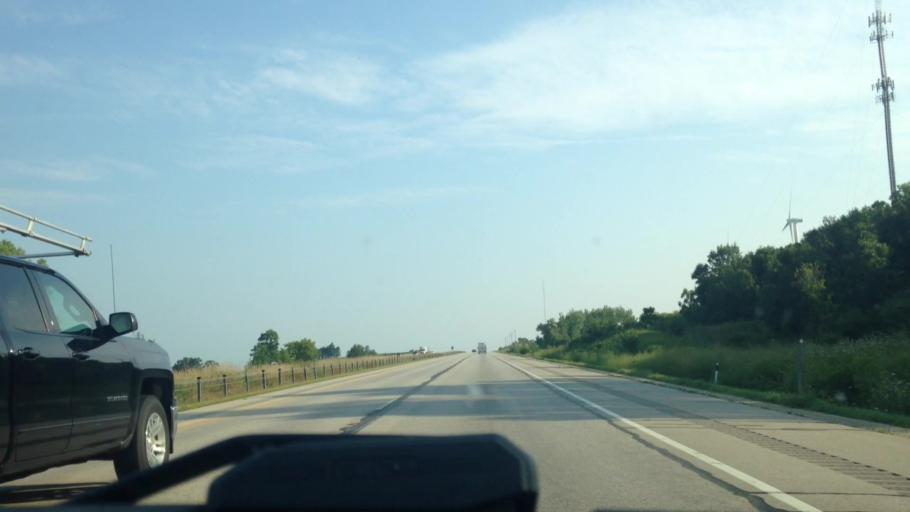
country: US
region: Wisconsin
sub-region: Dodge County
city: Lomira
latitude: 43.6517
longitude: -88.4414
